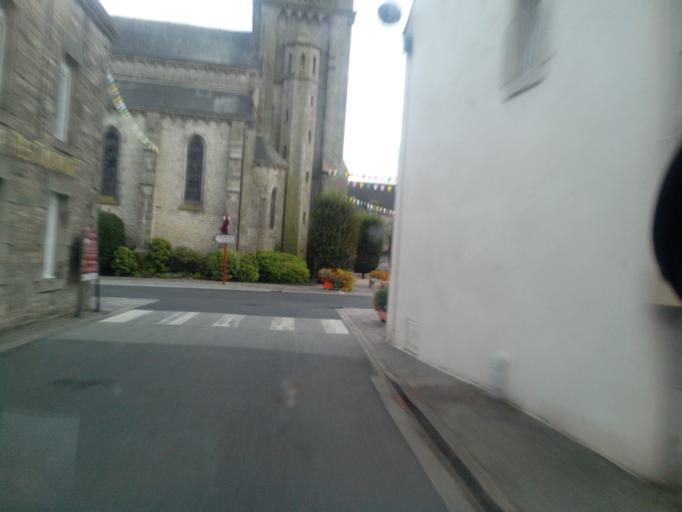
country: FR
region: Brittany
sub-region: Departement du Morbihan
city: Plumelec
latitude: 47.8382
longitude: -2.6405
